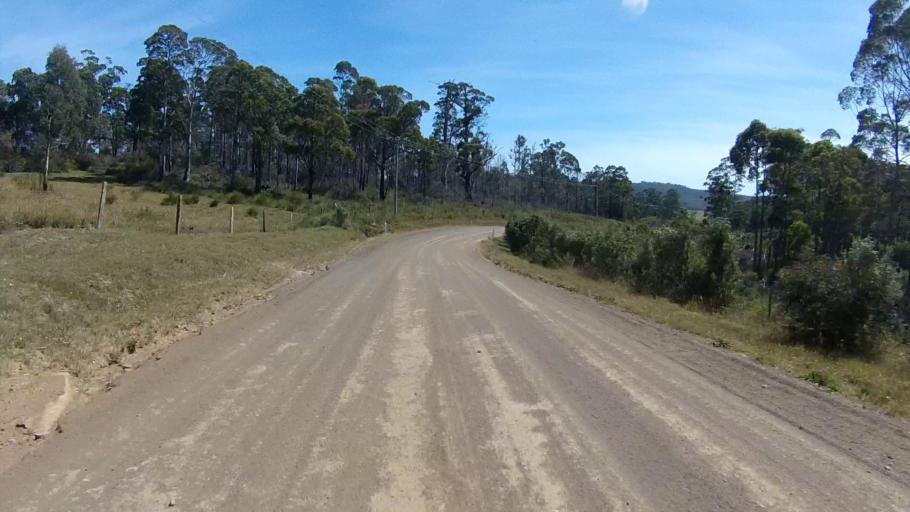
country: AU
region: Tasmania
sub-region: Sorell
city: Sorell
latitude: -42.7295
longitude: 147.7395
